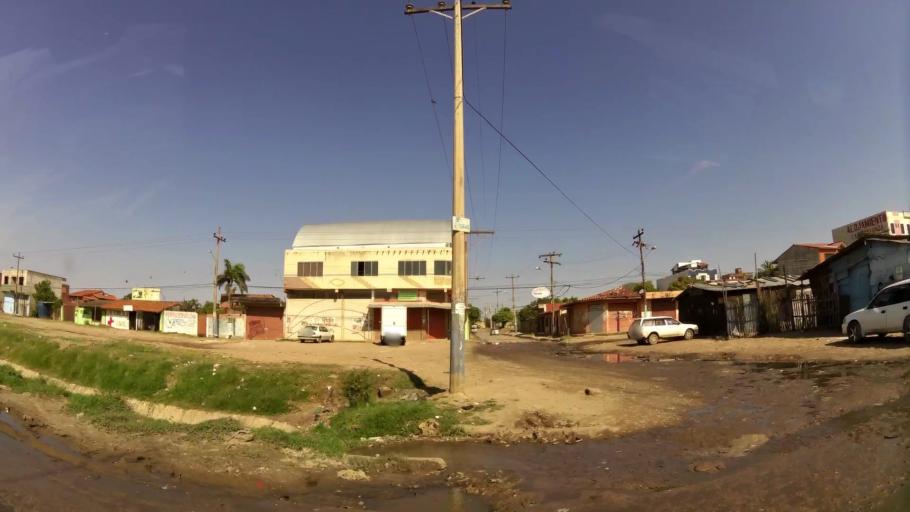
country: BO
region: Santa Cruz
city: Santa Cruz de la Sierra
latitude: -17.8241
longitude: -63.1300
